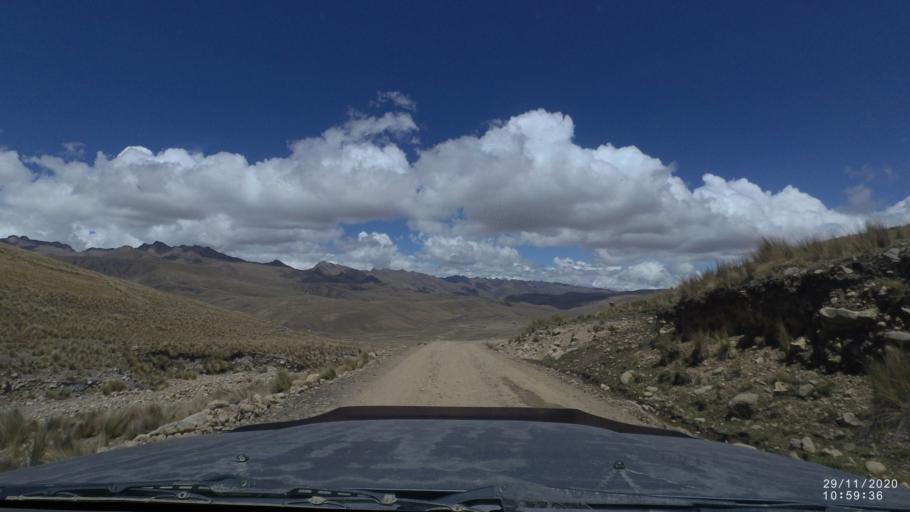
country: BO
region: Cochabamba
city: Cochabamba
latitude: -17.2076
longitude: -66.2276
